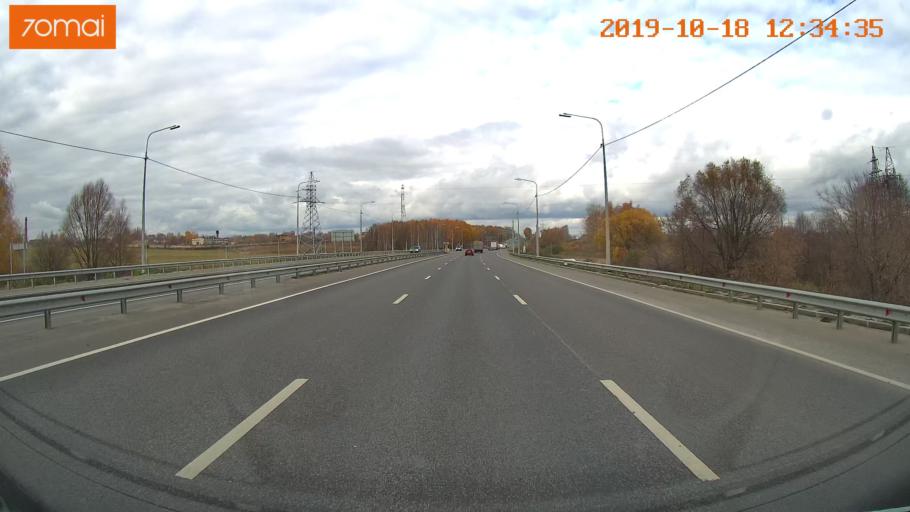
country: RU
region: Rjazan
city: Ryazan'
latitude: 54.6155
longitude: 39.6376
